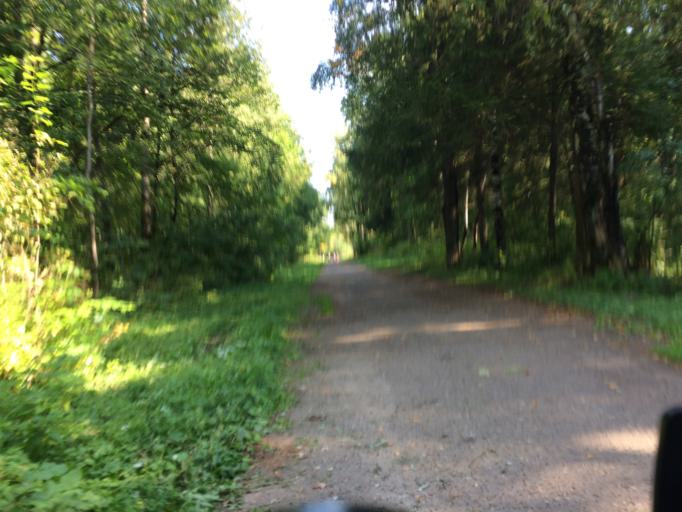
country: RU
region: Mariy-El
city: Yoshkar-Ola
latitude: 56.6175
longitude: 47.9354
